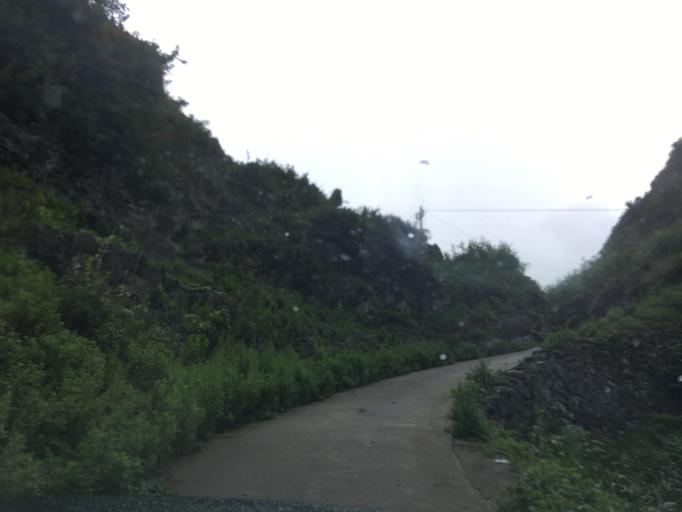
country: CN
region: Guangxi Zhuangzu Zizhiqu
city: Xinzhou
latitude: 24.9952
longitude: 105.6440
